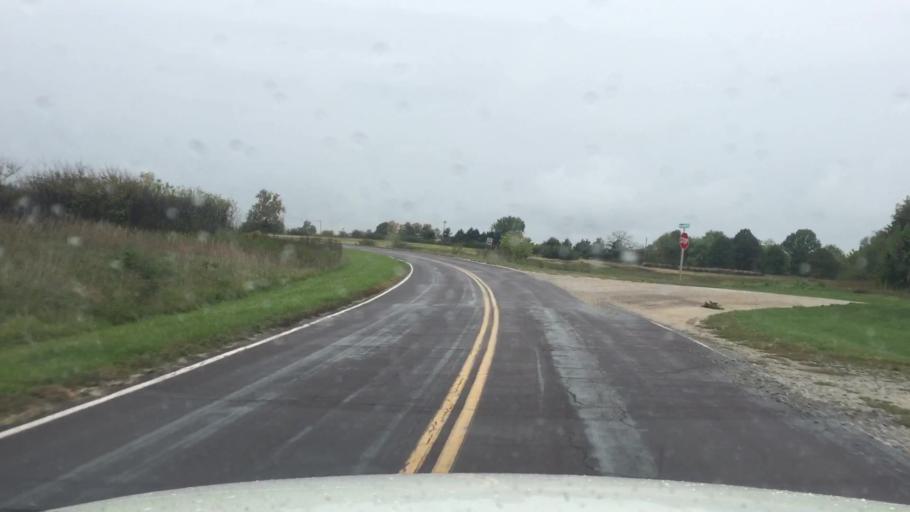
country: US
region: Missouri
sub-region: Boone County
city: Ashland
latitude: 38.7307
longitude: -92.2573
